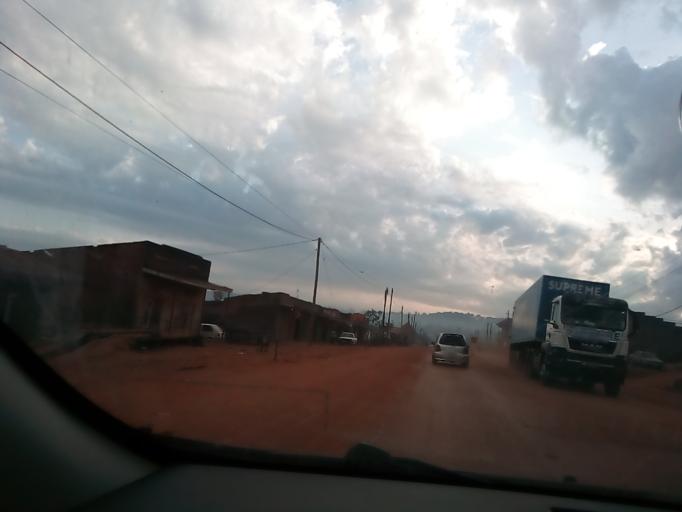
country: UG
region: Central Region
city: Masaka
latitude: -0.3228
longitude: 31.7555
